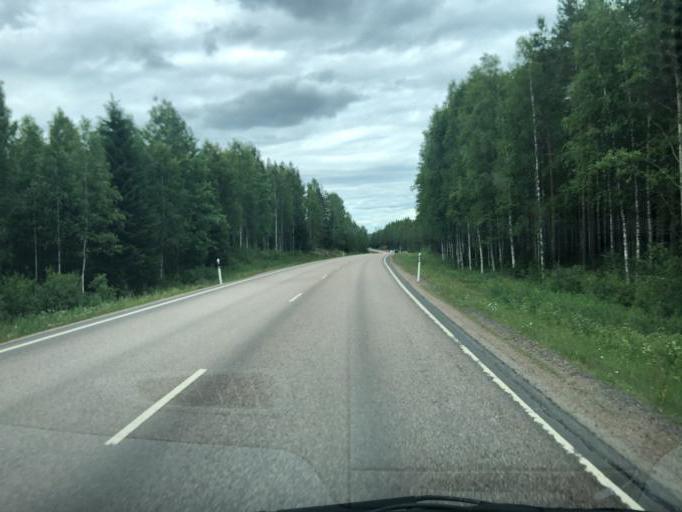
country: FI
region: Southern Savonia
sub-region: Mikkeli
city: Maentyharju
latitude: 61.1200
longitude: 27.0989
